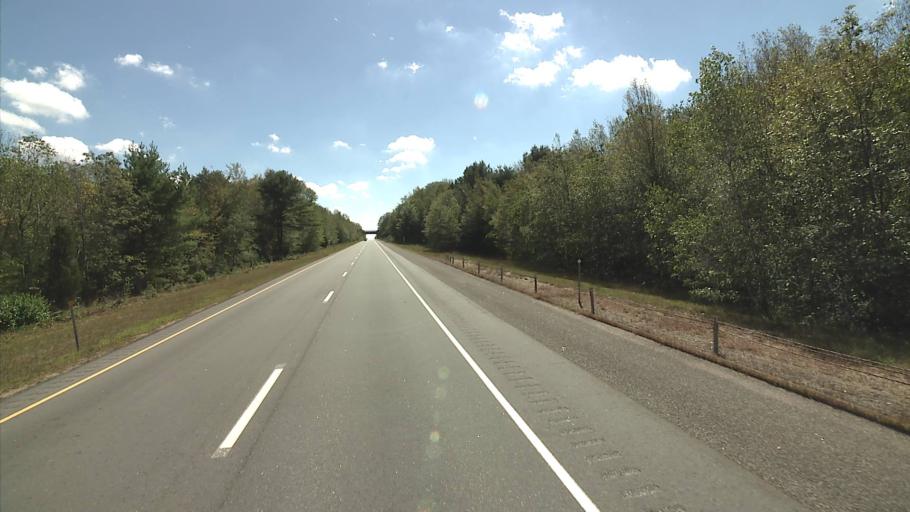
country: US
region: Connecticut
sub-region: New London County
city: Colchester
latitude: 41.5425
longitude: -72.3147
